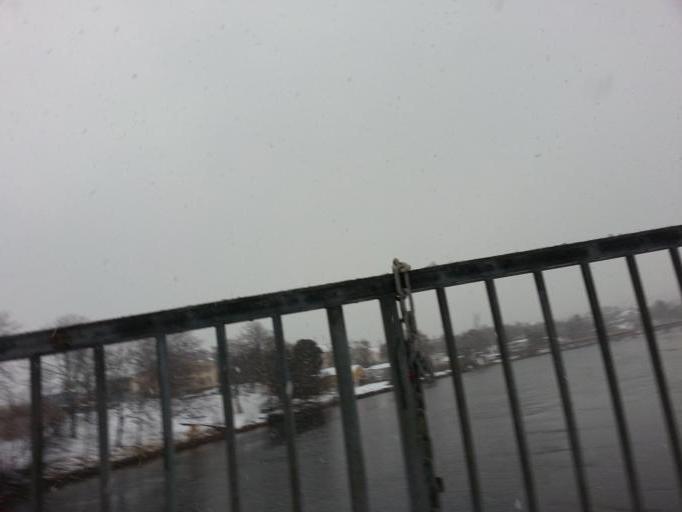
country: NO
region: Sor-Trondelag
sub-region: Trondheim
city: Trondheim
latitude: 63.4289
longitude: 10.3766
